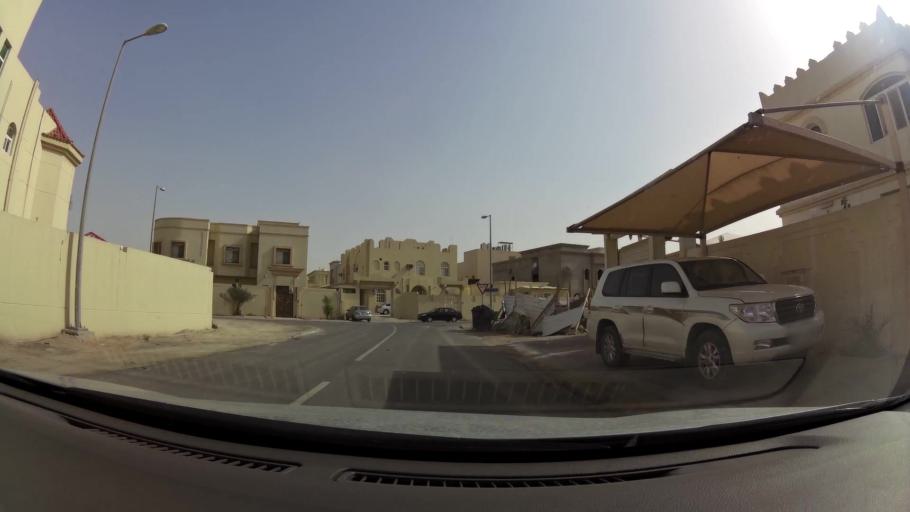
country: QA
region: Baladiyat ar Rayyan
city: Ar Rayyan
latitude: 25.2440
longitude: 51.4454
